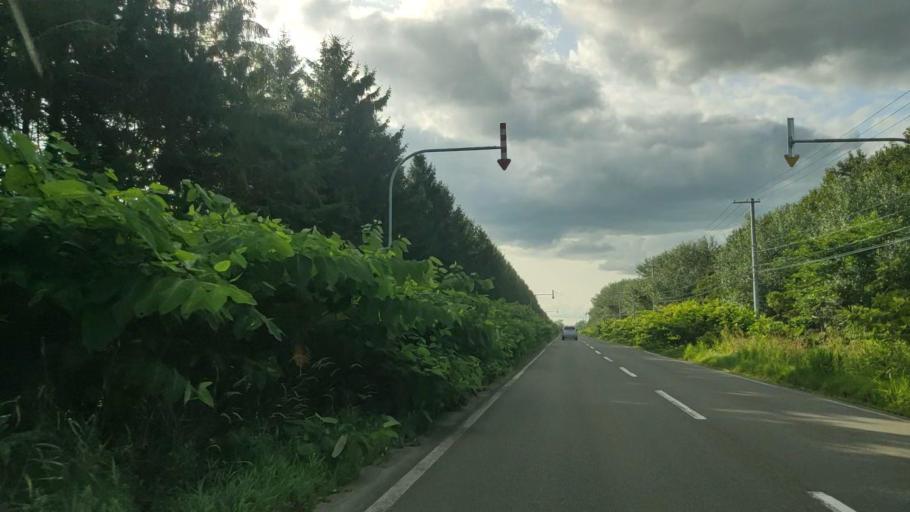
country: JP
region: Hokkaido
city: Makubetsu
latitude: 44.8995
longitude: 141.9133
